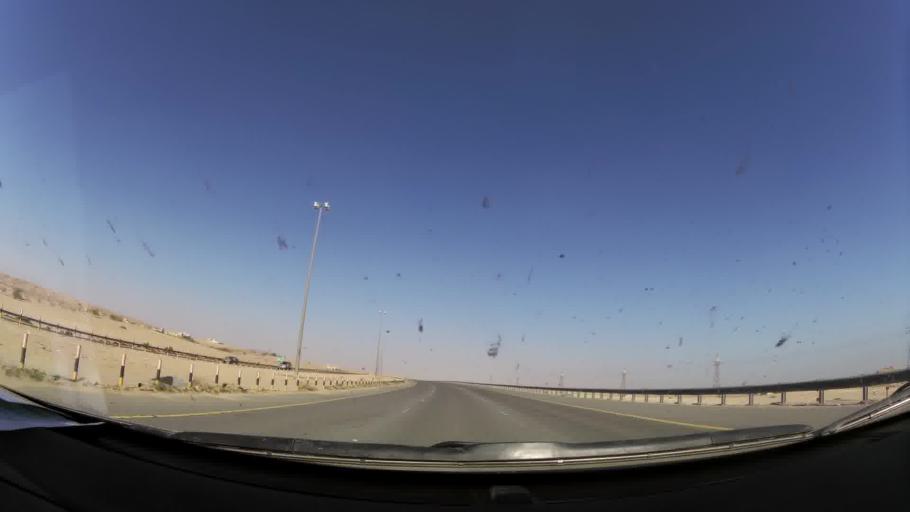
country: KW
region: Muhafazat al Jahra'
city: Al Jahra'
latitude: 29.4499
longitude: 47.7564
